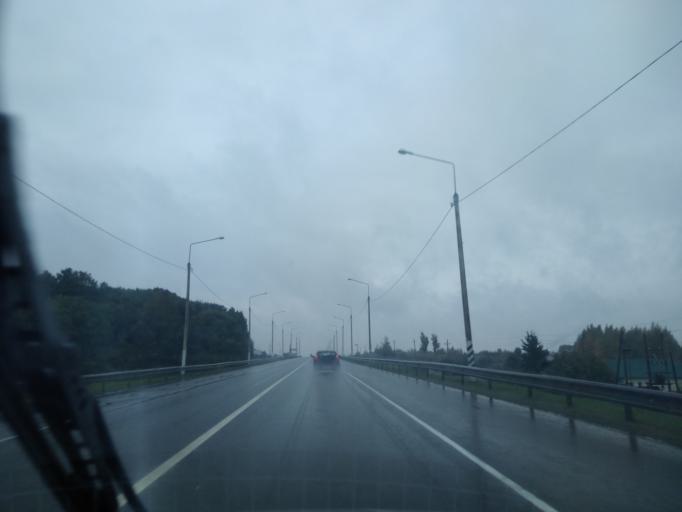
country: RU
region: Tula
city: Shchekino
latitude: 54.0047
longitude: 37.4762
